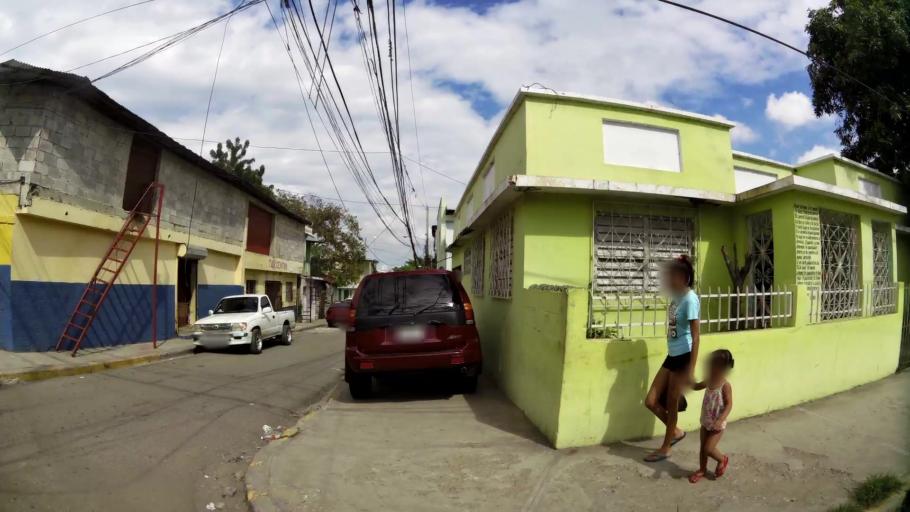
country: DO
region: Santiago
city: Santiago de los Caballeros
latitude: 19.4848
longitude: -70.7300
